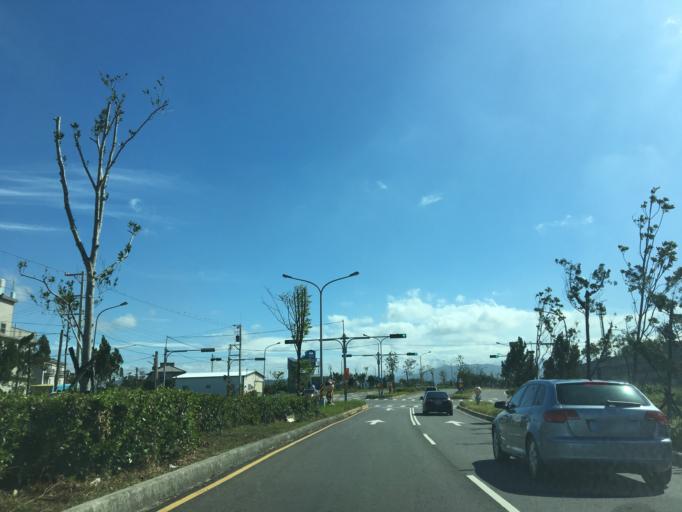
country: TW
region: Taiwan
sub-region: Hsinchu
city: Zhubei
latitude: 24.7818
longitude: 121.0489
